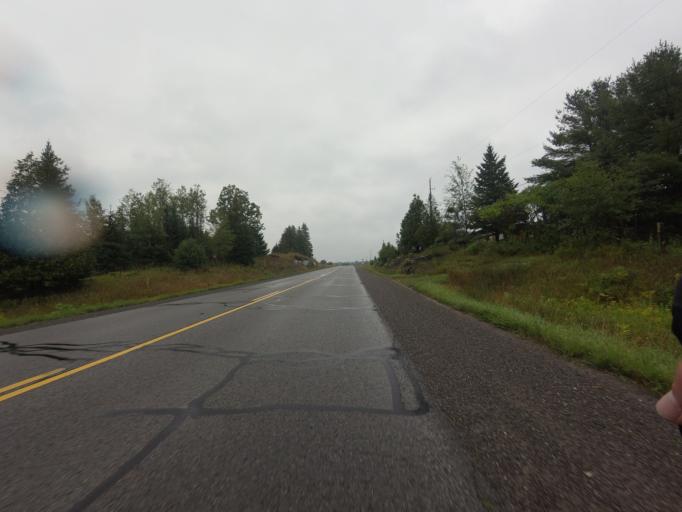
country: CA
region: Ontario
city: Perth
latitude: 45.0857
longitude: -76.4325
